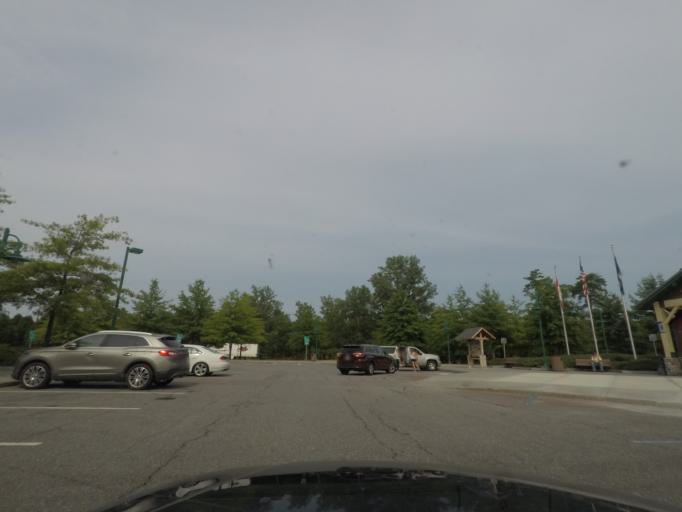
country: US
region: New York
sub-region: Clinton County
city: Peru
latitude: 44.6045
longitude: -73.4913
